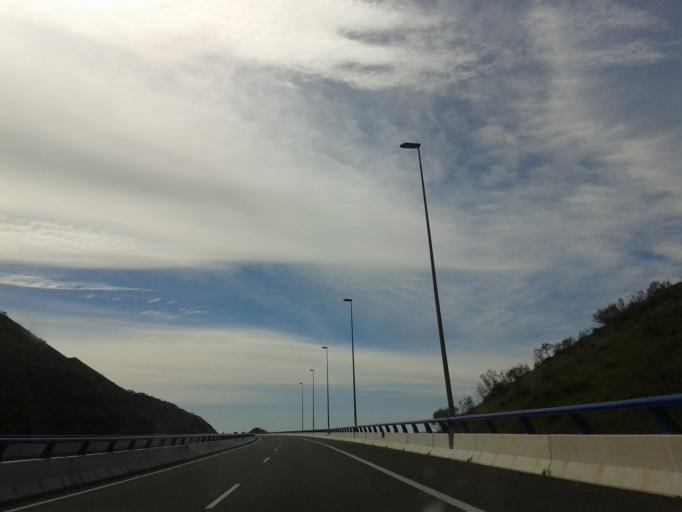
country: ES
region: Andalusia
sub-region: Provincia de Malaga
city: Almogia
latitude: 36.8566
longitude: -4.4852
